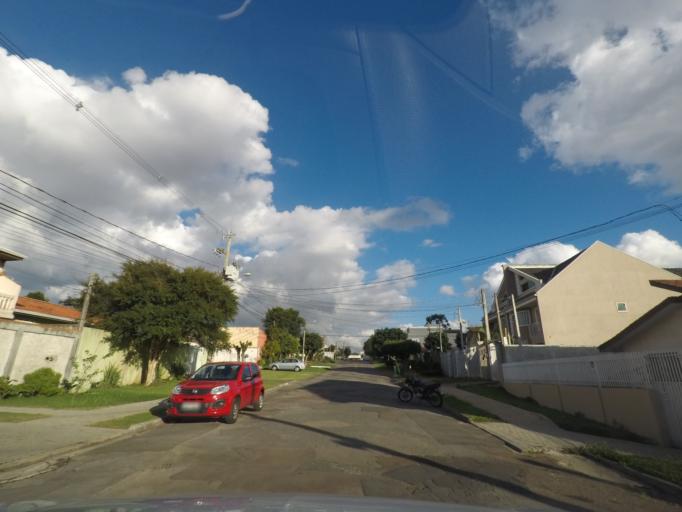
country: BR
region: Parana
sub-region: Sao Jose Dos Pinhais
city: Sao Jose dos Pinhais
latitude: -25.4984
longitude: -49.2544
